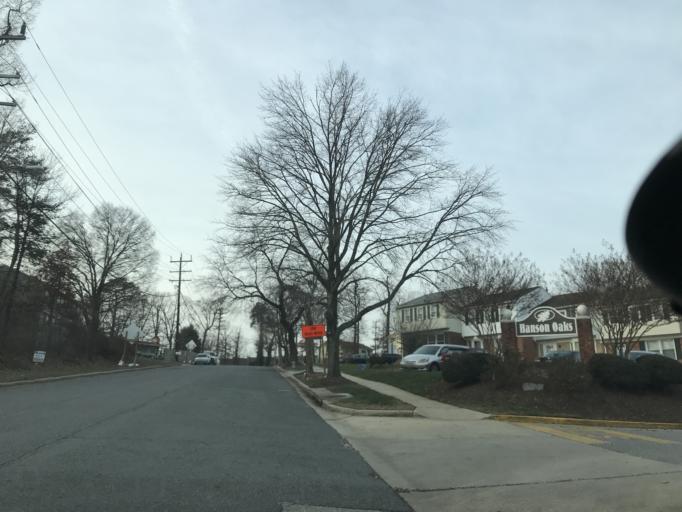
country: US
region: Maryland
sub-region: Prince George's County
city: Woodlawn
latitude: 38.9458
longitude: -76.8783
